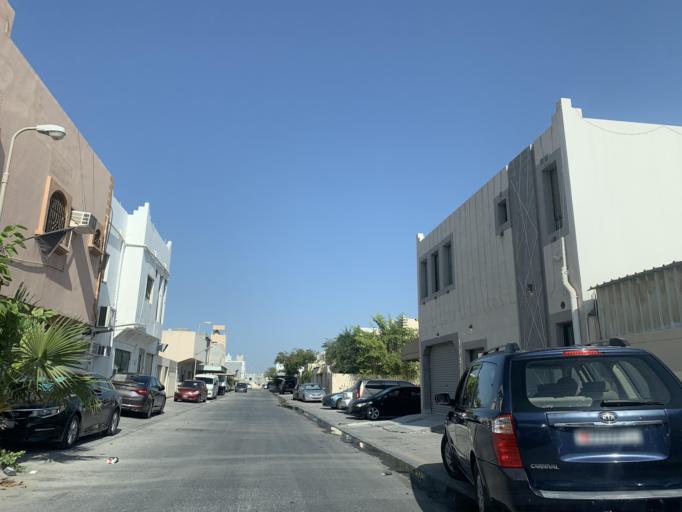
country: BH
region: Central Governorate
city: Madinat Hamad
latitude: 26.1270
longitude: 50.4798
